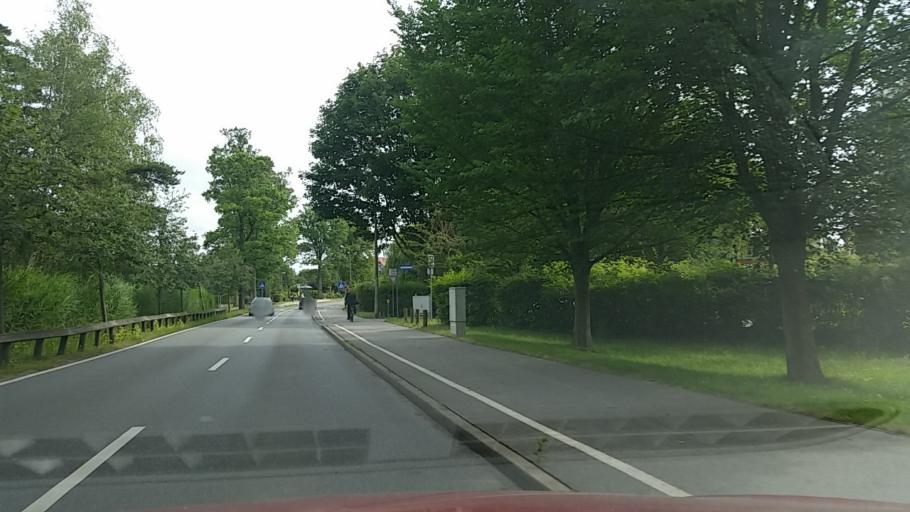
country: DE
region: Mecklenburg-Vorpommern
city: Ostseebad Kuhlungsborn
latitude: 54.1438
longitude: 11.7544
